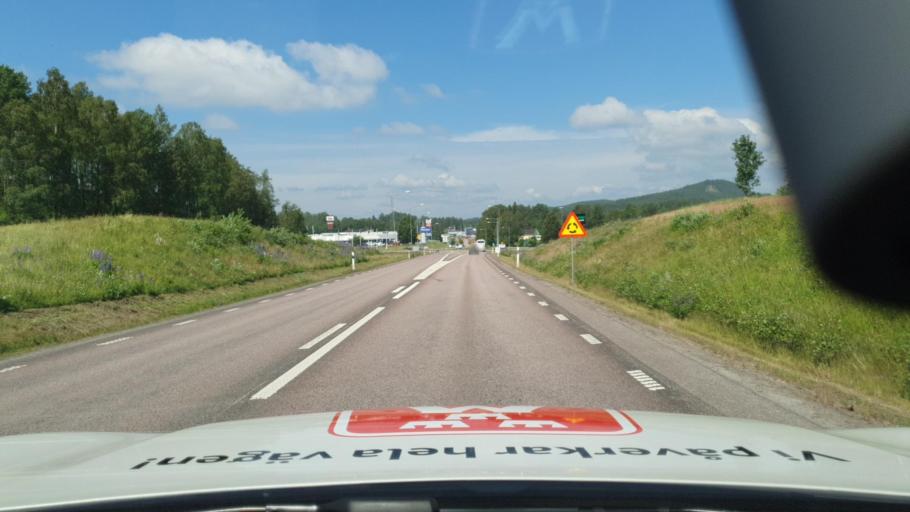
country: SE
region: Vaermland
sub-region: Torsby Kommun
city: Torsby
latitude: 60.1282
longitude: 12.9995
